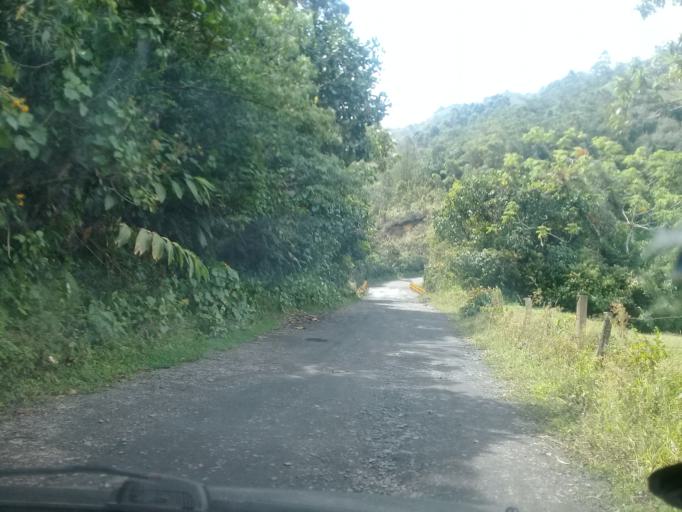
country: CO
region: Cundinamarca
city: Gachala
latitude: 4.6946
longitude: -73.4703
